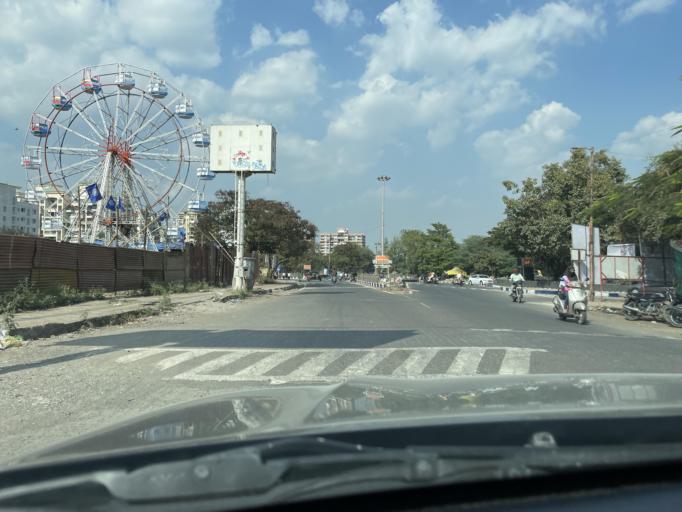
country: IN
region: Maharashtra
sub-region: Pune Division
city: Pune
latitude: 18.4851
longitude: 73.9004
